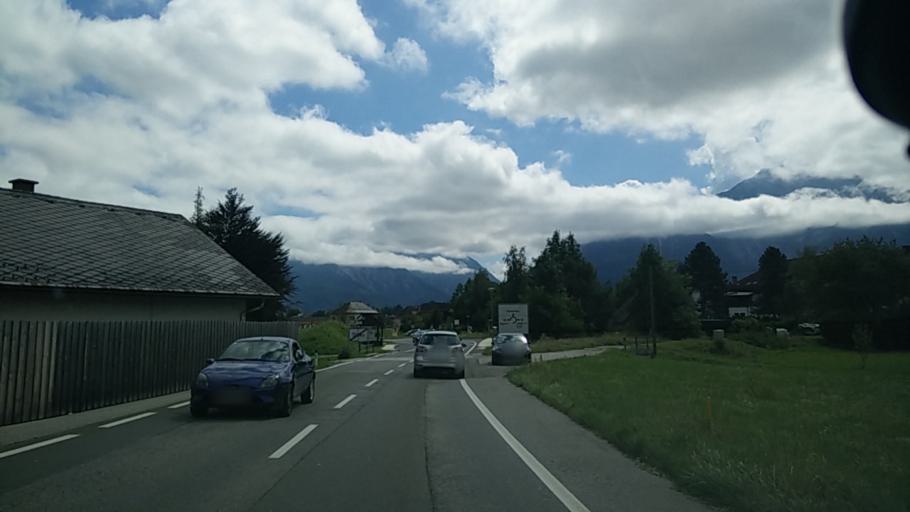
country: AT
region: Carinthia
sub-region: Politischer Bezirk Klagenfurt Land
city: Maria Rain
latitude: 46.5372
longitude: 14.2632
